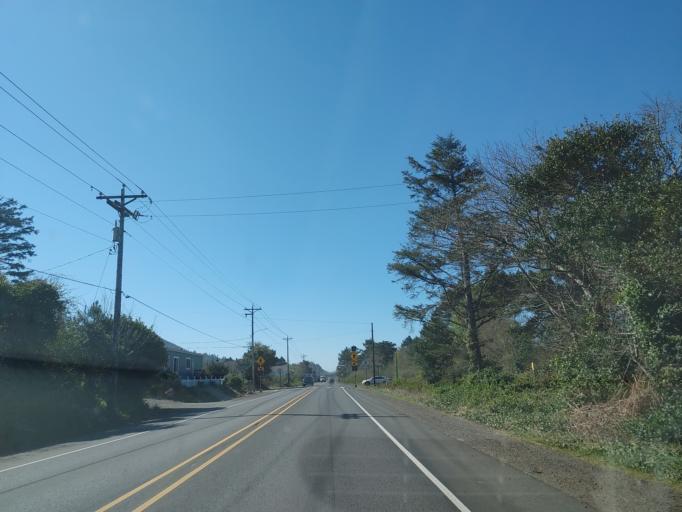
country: US
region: Oregon
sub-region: Tillamook County
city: Rockaway Beach
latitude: 45.6009
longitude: -123.9460
